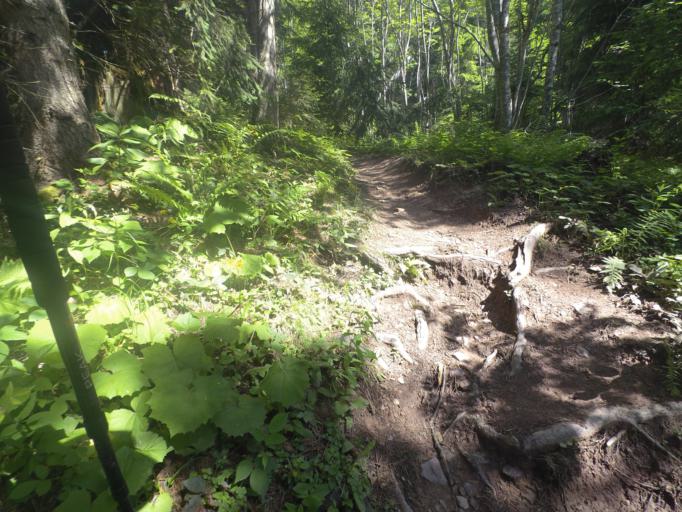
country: AT
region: Salzburg
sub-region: Politischer Bezirk Zell am See
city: Leogang
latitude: 47.4559
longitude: 12.7692
